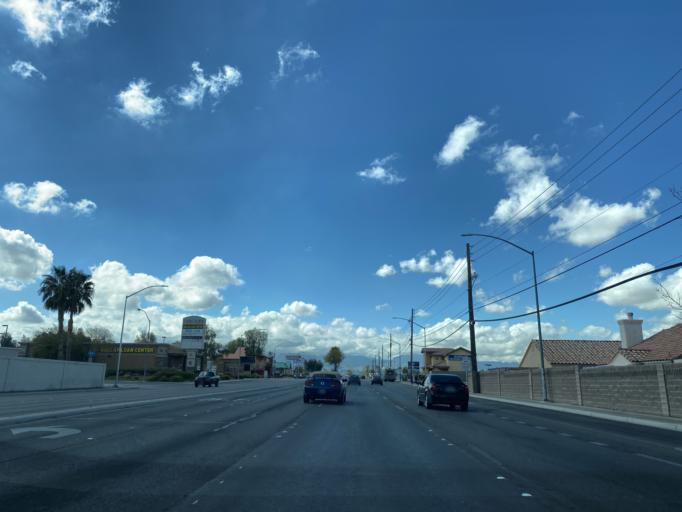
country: US
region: Nevada
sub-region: Clark County
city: North Las Vegas
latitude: 36.2395
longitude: -115.1746
